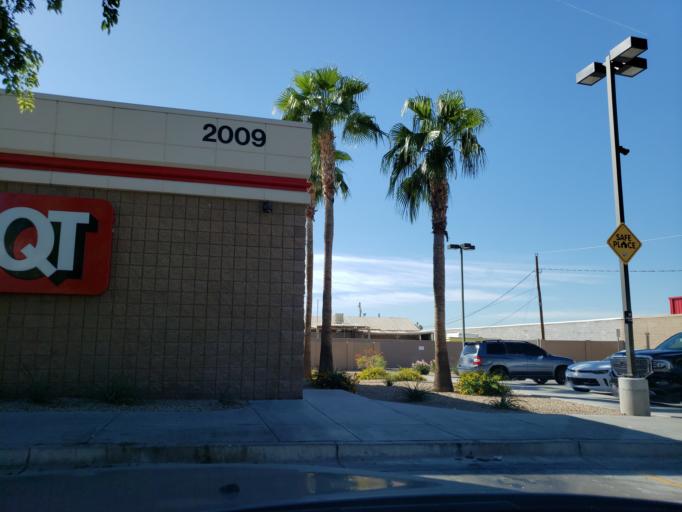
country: US
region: Arizona
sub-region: Maricopa County
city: Glendale
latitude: 33.5382
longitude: -112.1020
